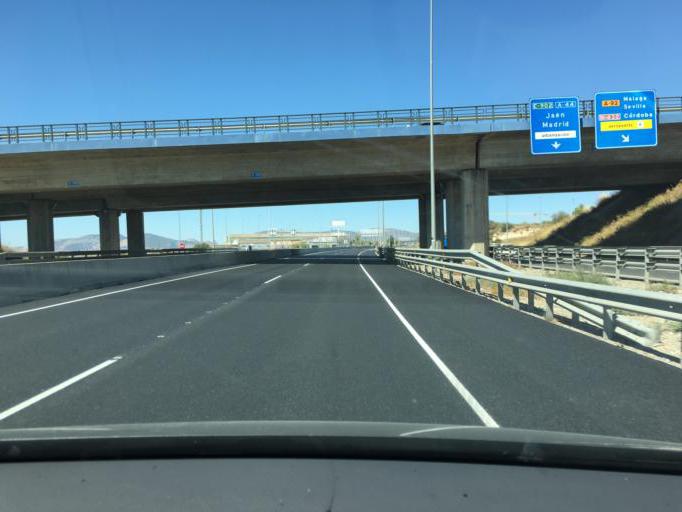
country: ES
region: Andalusia
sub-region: Provincia de Granada
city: Albolote
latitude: 37.2410
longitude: -3.6515
